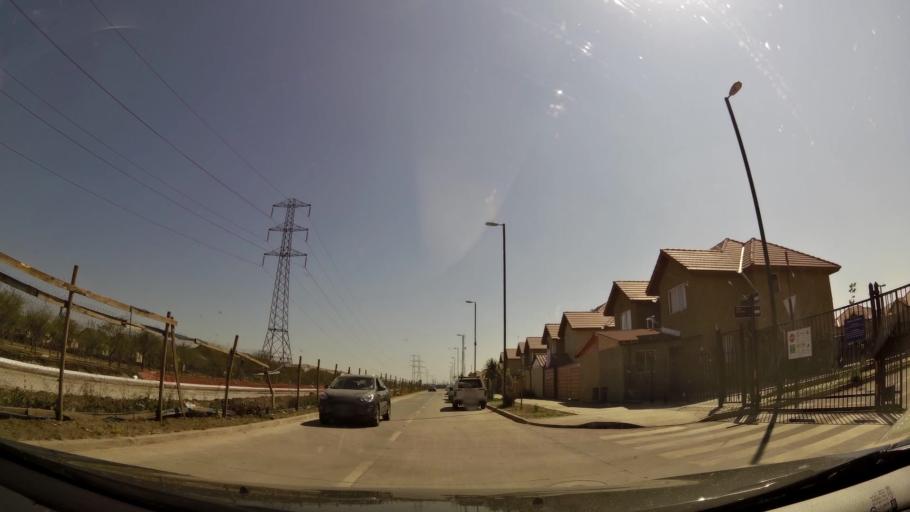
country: CL
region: Santiago Metropolitan
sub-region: Provincia de Chacabuco
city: Chicureo Abajo
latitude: -33.3238
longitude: -70.7557
